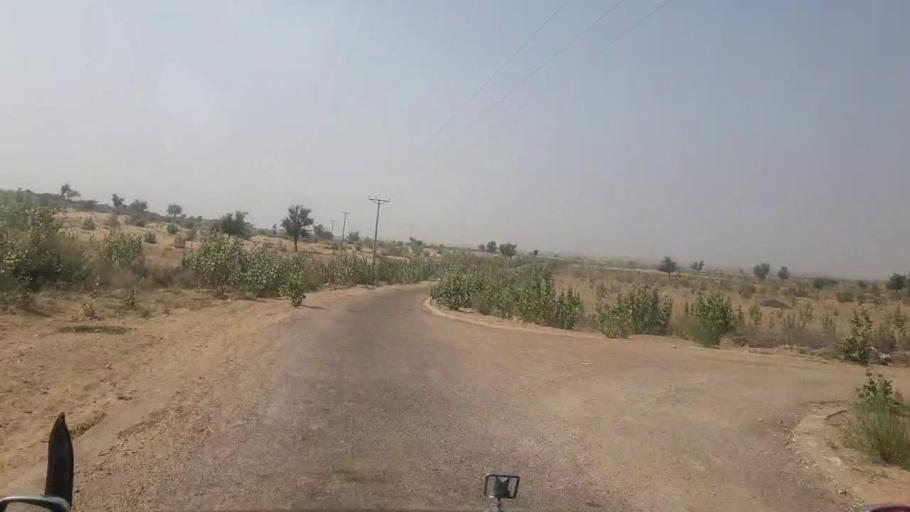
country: PK
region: Sindh
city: Islamkot
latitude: 25.0973
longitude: 70.1794
